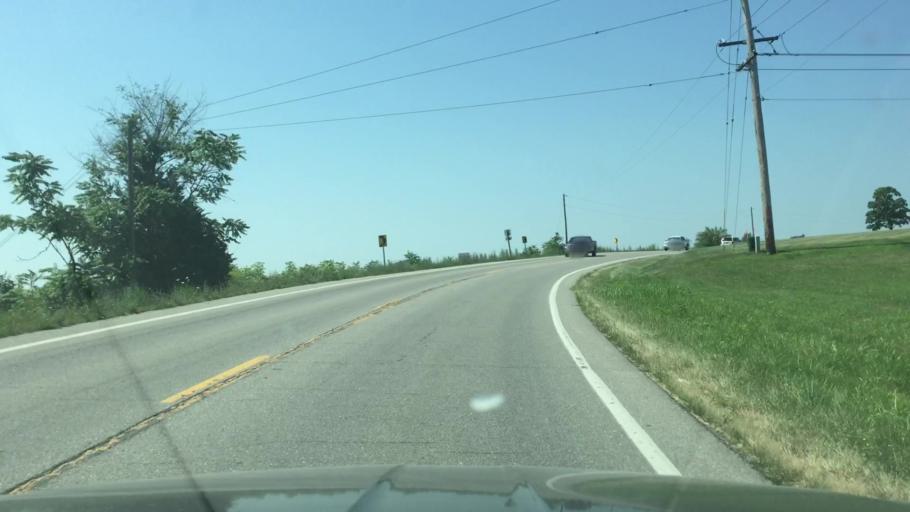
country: US
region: Missouri
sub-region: Moniteau County
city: Tipton
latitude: 38.6439
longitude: -92.7842
